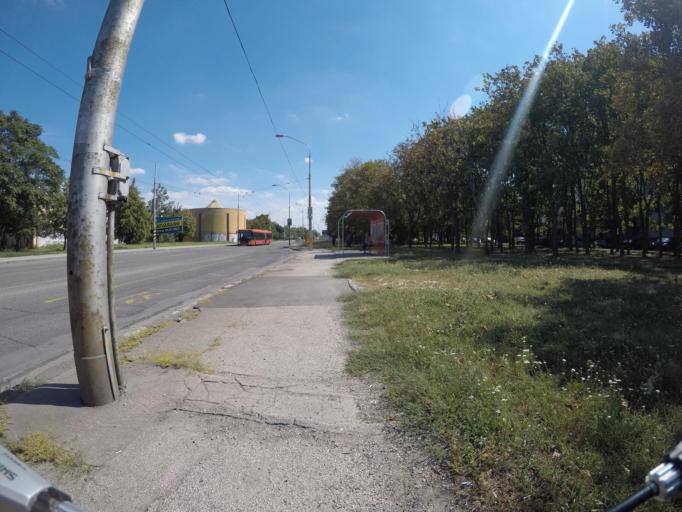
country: SK
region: Bratislavsky
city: Dunajska Luzna
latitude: 48.1420
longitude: 17.2142
